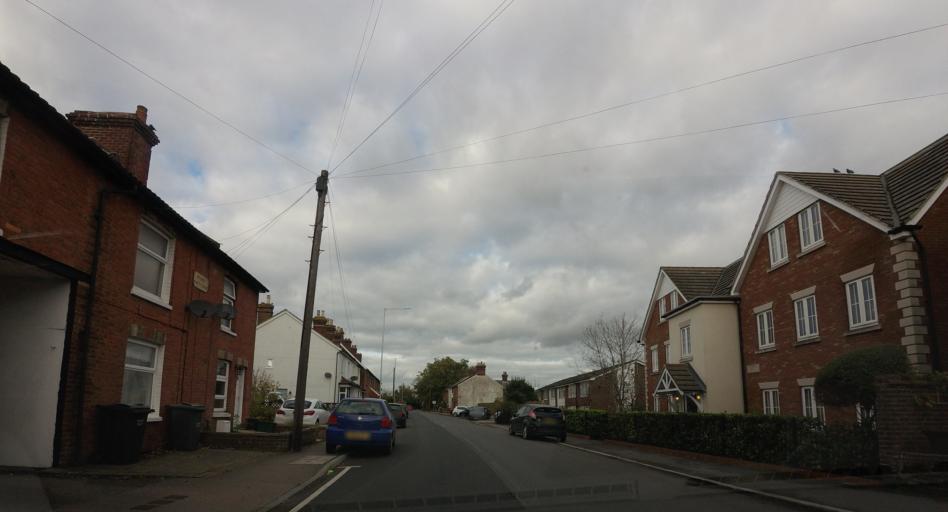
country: GB
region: England
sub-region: Kent
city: Tonbridge
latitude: 51.2065
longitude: 0.2778
